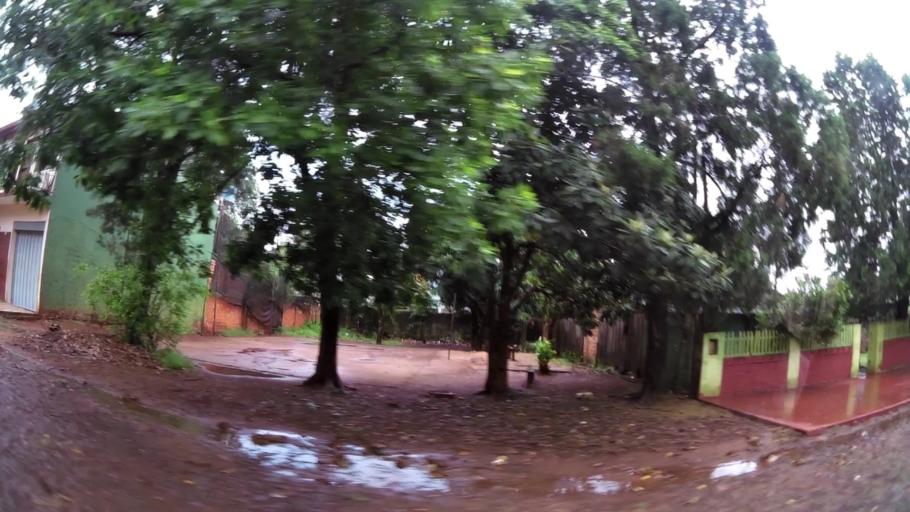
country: PY
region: Alto Parana
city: Presidente Franco
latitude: -25.5162
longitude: -54.6729
